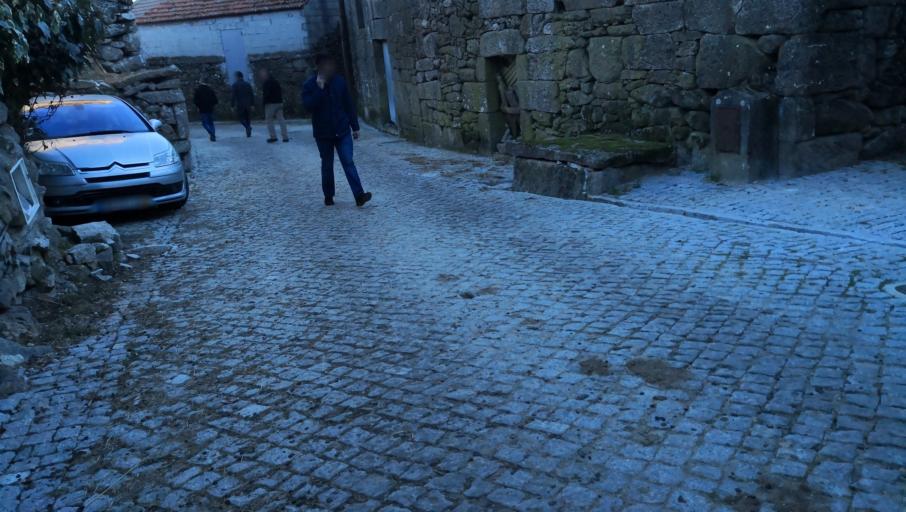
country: PT
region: Vila Real
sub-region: Ribeira de Pena
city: Ribeira de Pena
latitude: 41.5040
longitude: -7.7429
